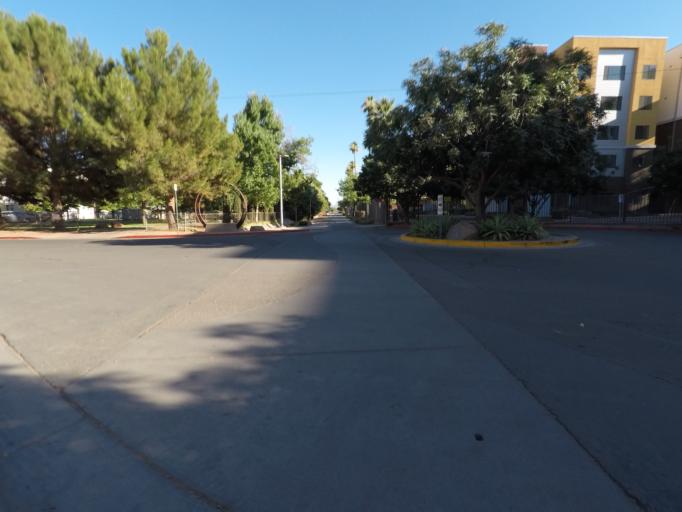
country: US
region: Arizona
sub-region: Maricopa County
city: Glendale
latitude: 33.5133
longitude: -112.1257
